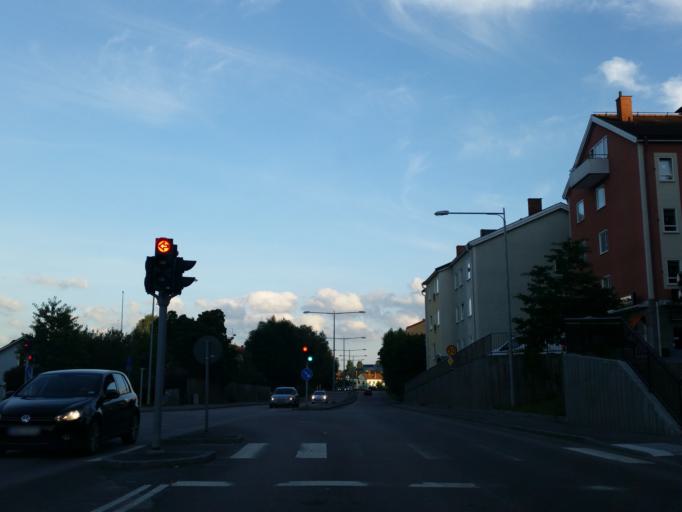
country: SE
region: Stockholm
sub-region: Sodertalje Kommun
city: Soedertaelje
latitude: 59.2003
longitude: 17.6176
